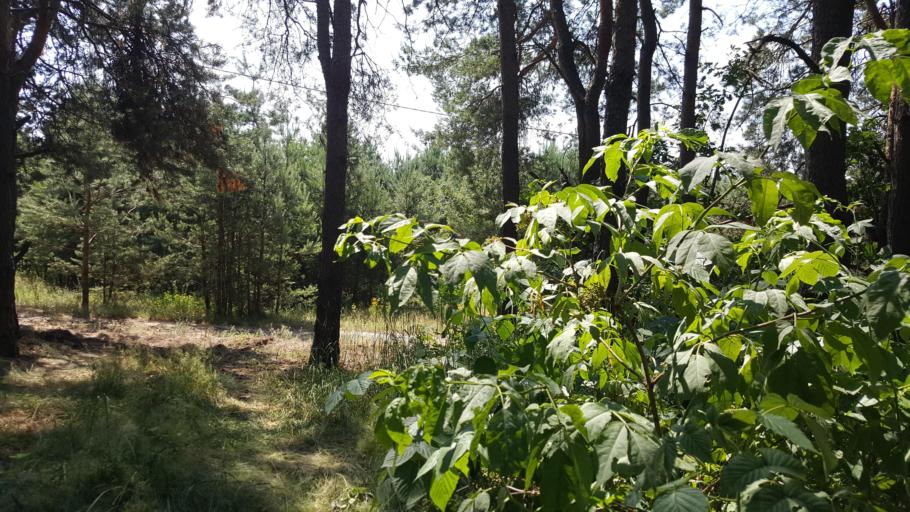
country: BY
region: Brest
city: Kamyanyets
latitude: 52.4070
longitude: 23.8419
